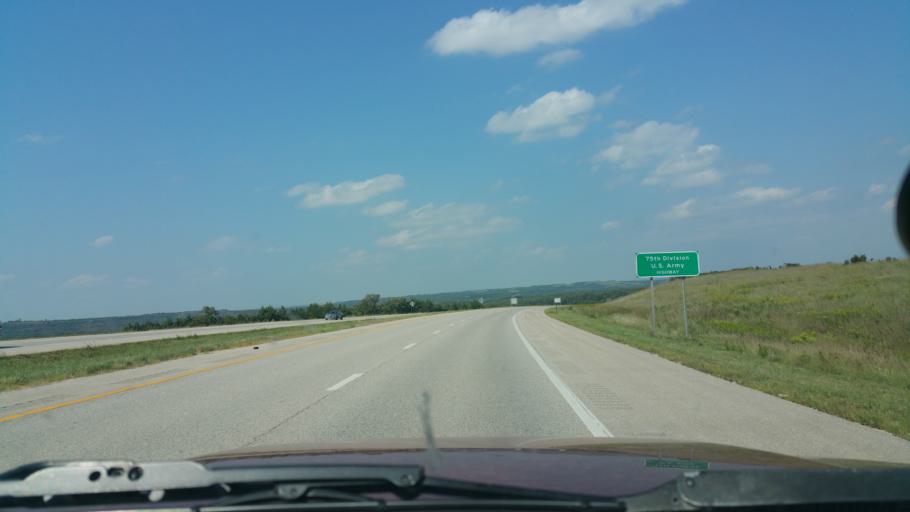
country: US
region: Kansas
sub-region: Geary County
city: Grandview Plaza
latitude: 39.0647
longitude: -96.7432
